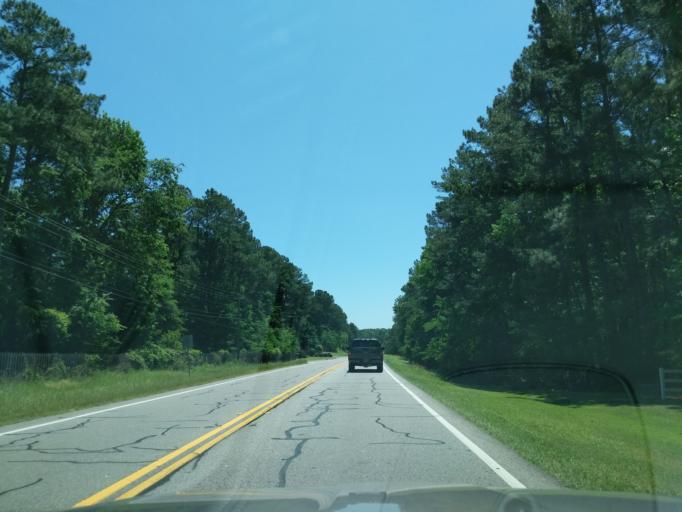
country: US
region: Georgia
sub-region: Columbia County
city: Evans
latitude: 33.5658
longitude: -82.1111
